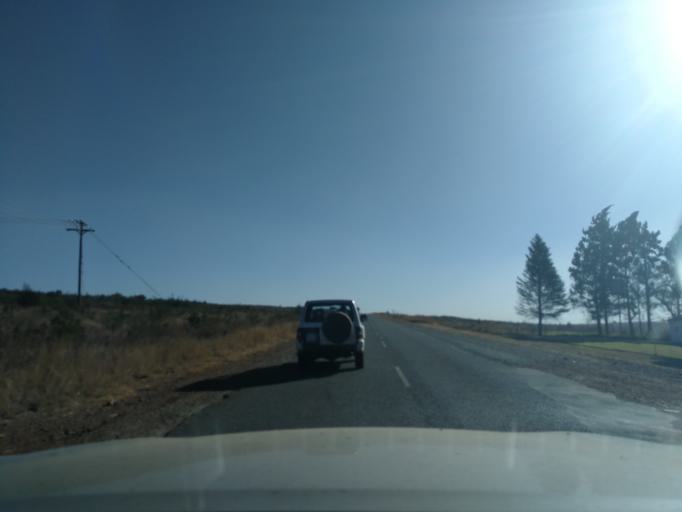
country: ZA
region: Gauteng
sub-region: West Rand District Municipality
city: Krugersdorp
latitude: -25.9795
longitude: 27.6727
